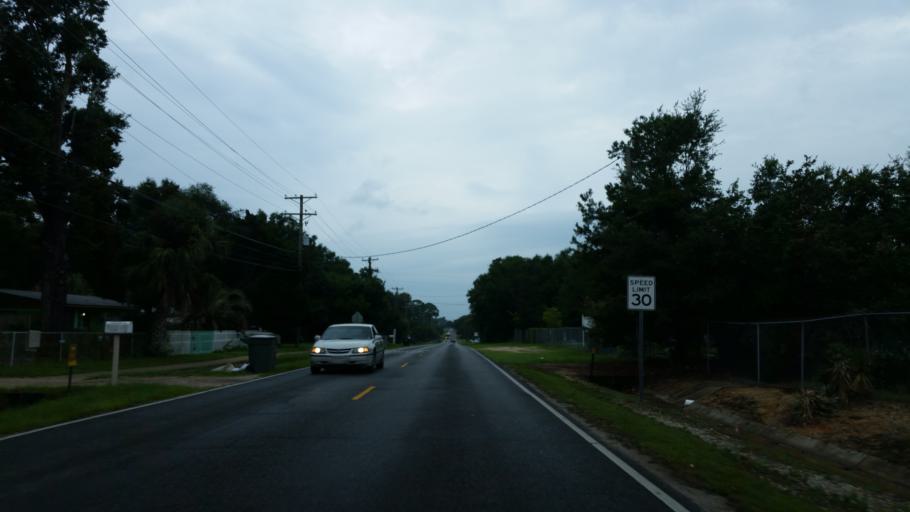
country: US
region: Florida
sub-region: Escambia County
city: Warrington
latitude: 30.4034
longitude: -87.2742
